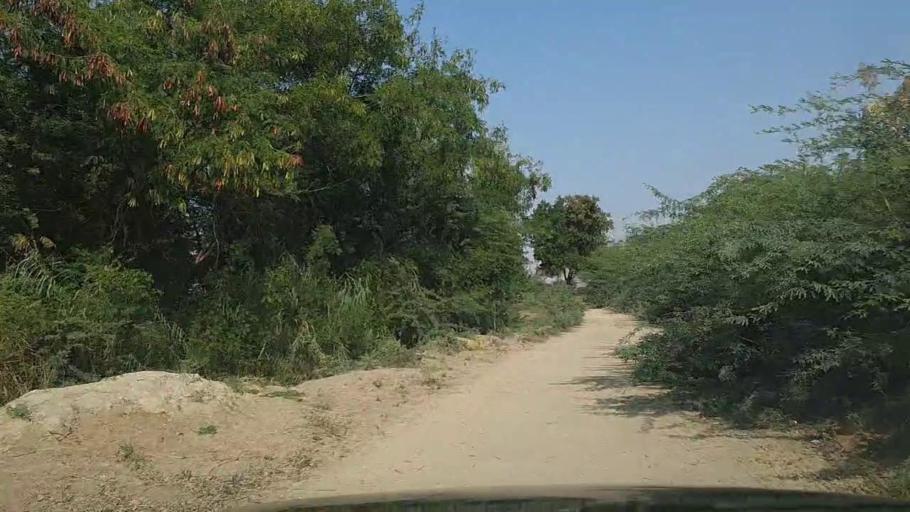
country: PK
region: Sindh
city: Mirpur Sakro
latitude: 24.6186
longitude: 67.7792
